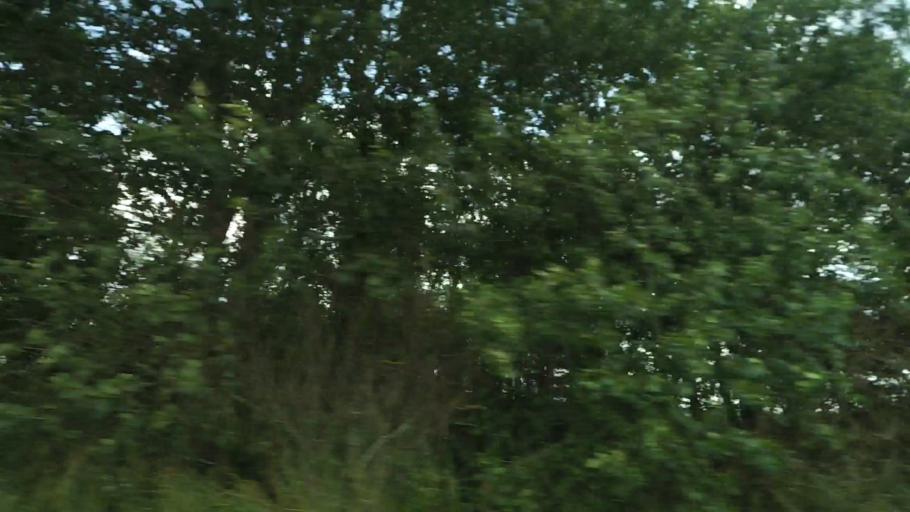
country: DK
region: Central Jutland
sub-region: Norddjurs Kommune
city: Auning
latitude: 56.5041
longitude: 10.4248
